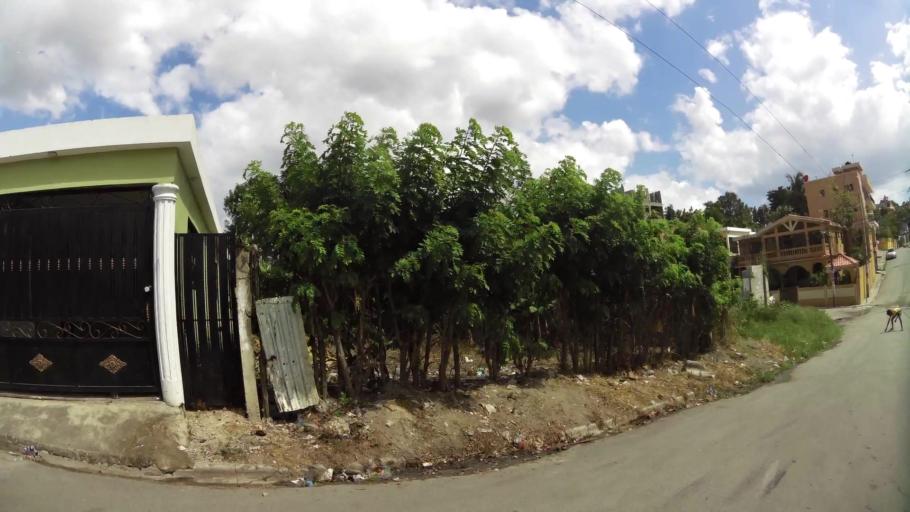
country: DO
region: Nacional
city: Ensanche Luperon
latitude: 18.5338
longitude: -69.9083
